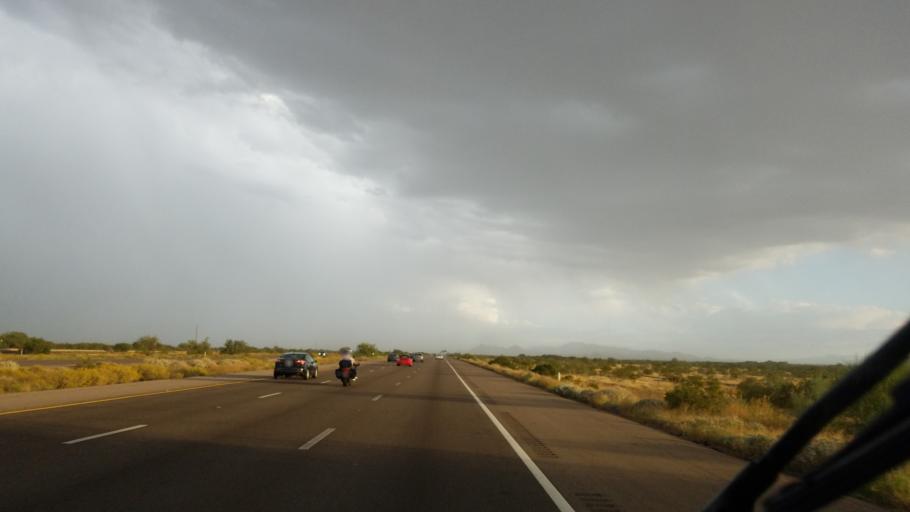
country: US
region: Arizona
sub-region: Pima County
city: Avra Valley
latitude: 32.5304
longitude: -111.2873
